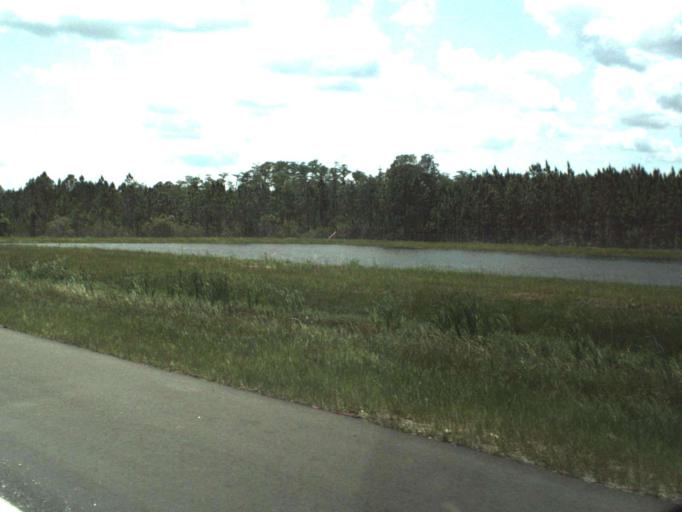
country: US
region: Florida
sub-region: Volusia County
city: Samsula-Spruce Creek
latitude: 29.0957
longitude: -81.1582
